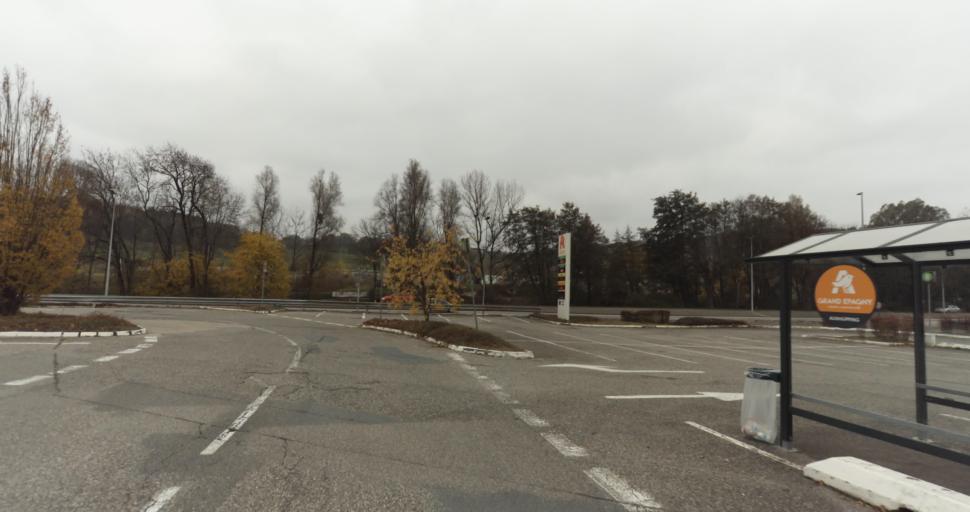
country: FR
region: Rhone-Alpes
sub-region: Departement de la Haute-Savoie
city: Poisy
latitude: 45.9377
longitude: 6.0725
